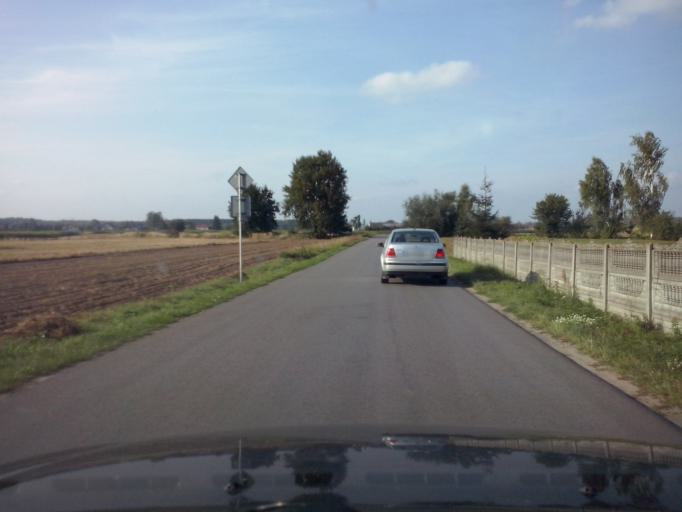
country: PL
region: Subcarpathian Voivodeship
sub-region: Powiat nizanski
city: Krzeszow
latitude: 50.3713
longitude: 22.3265
